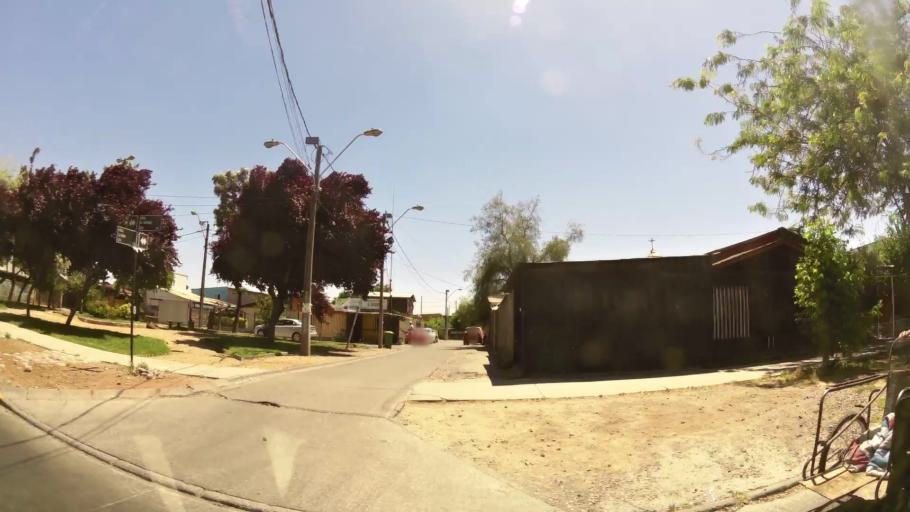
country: CL
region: Santiago Metropolitan
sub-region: Provincia de Santiago
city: La Pintana
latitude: -33.5727
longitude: -70.6659
